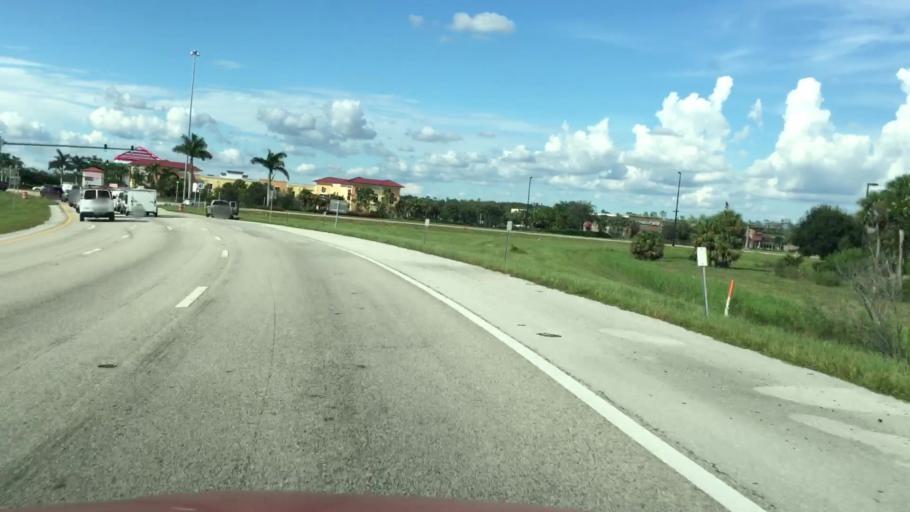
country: US
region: Florida
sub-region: Lee County
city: Three Oaks
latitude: 26.4916
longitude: -81.7917
